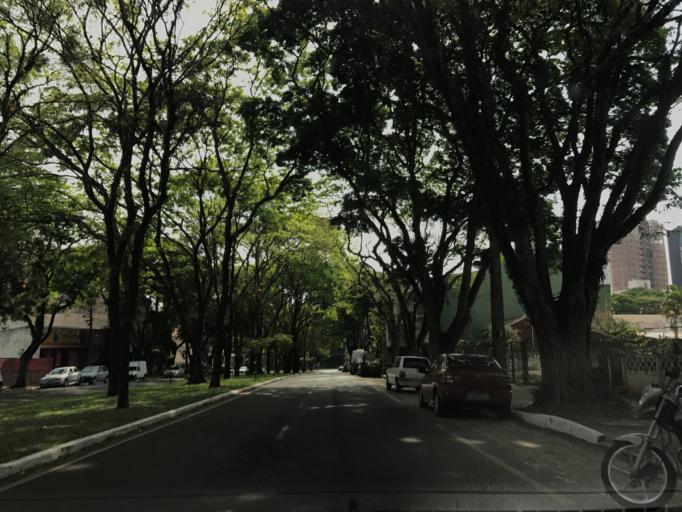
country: BR
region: Parana
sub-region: Maringa
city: Maringa
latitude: -23.4262
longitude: -51.9254
